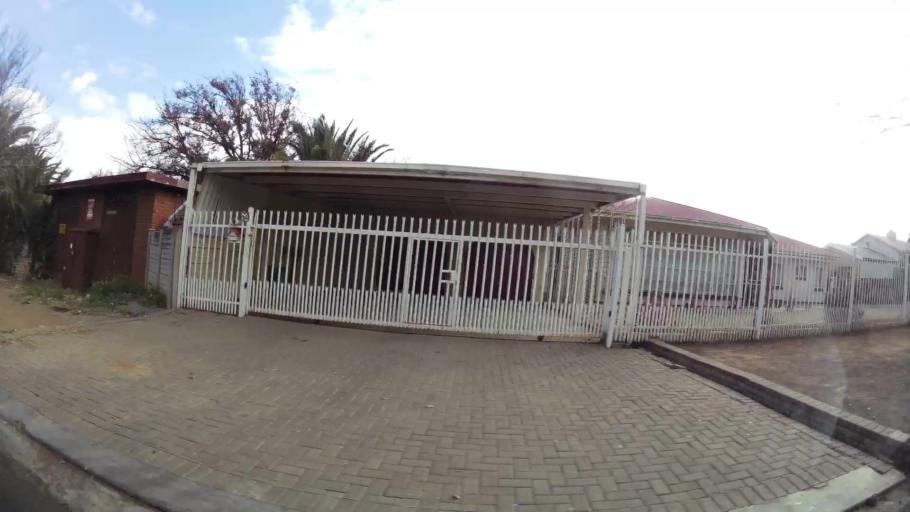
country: ZA
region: Orange Free State
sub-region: Mangaung Metropolitan Municipality
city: Bloemfontein
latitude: -29.0793
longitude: 26.2446
